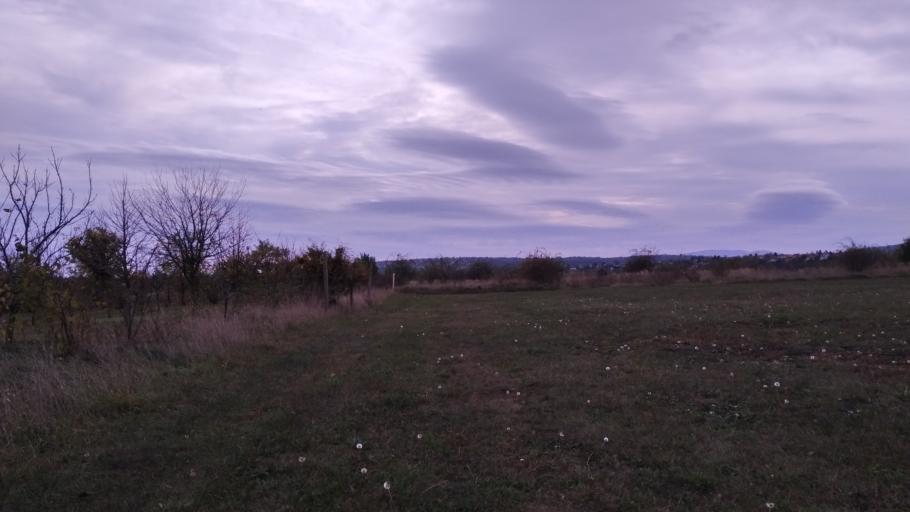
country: HU
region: Pest
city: Pomaz
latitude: 47.6396
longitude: 19.0480
